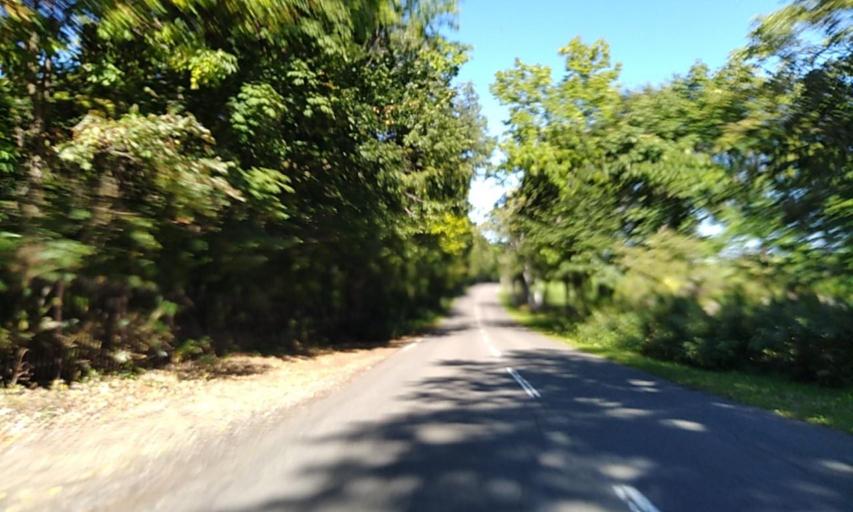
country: JP
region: Hokkaido
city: Sapporo
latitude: 42.9989
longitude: 141.3923
